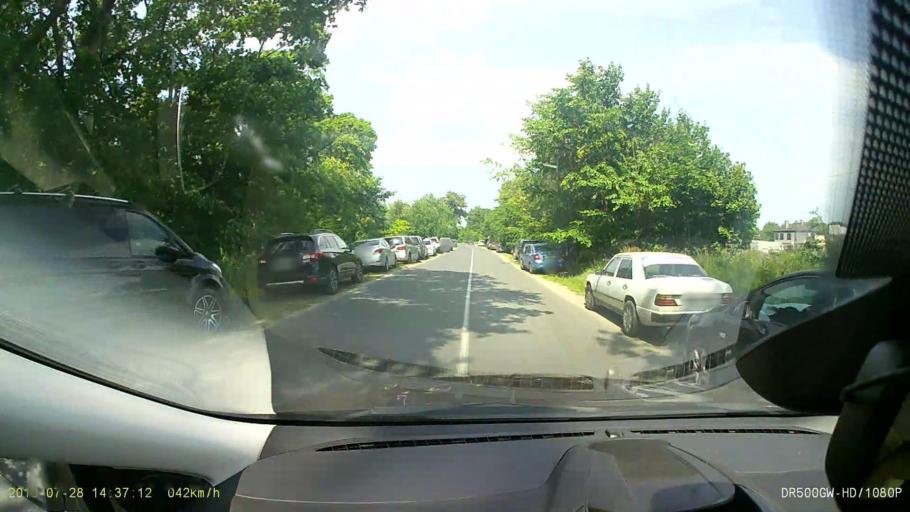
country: RU
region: Kaliningrad
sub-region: Gorod Kaliningrad
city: Yantarnyy
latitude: 54.8668
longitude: 19.9419
